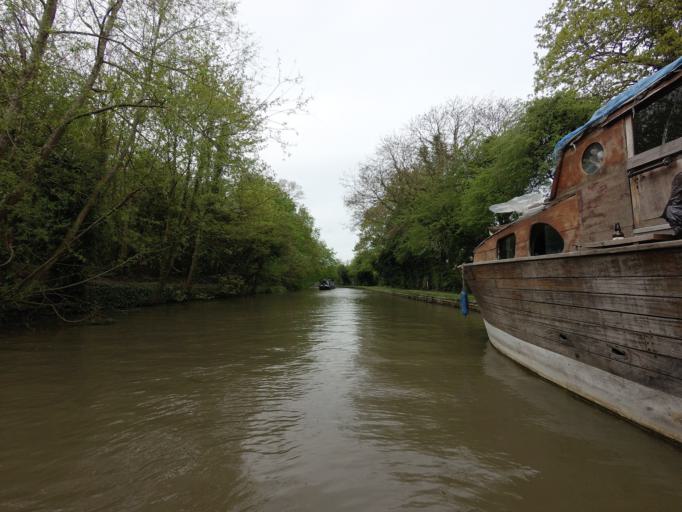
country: GB
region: England
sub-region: Milton Keynes
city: Bradwell
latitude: 52.0631
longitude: -0.8038
